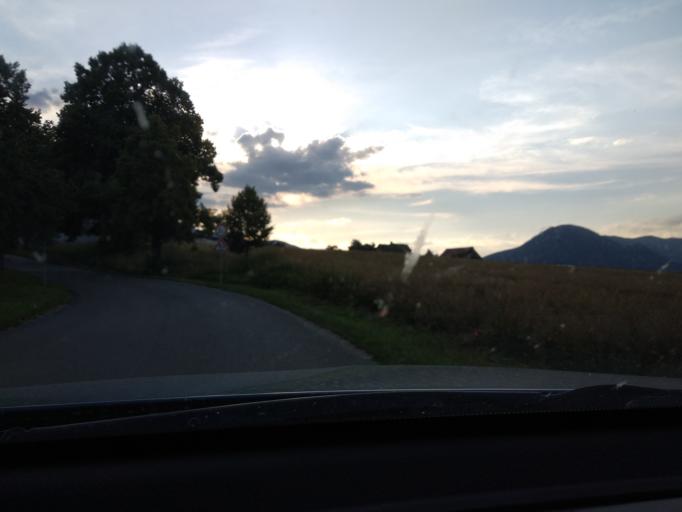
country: SK
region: Zilinsky
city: Ruzomberok
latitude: 49.0637
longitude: 19.3309
